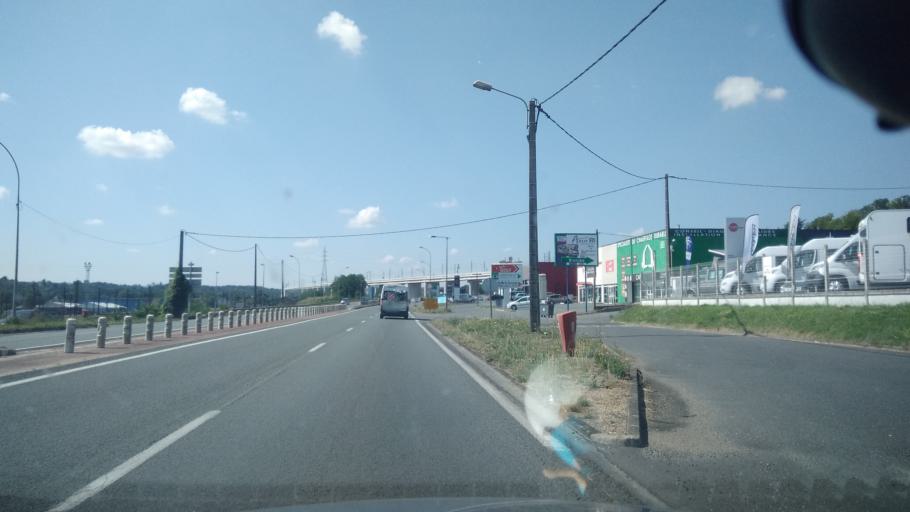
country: FR
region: Poitou-Charentes
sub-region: Departement de la Vienne
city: Chasseneuil-du-Poitou
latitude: 46.6261
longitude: 0.3543
